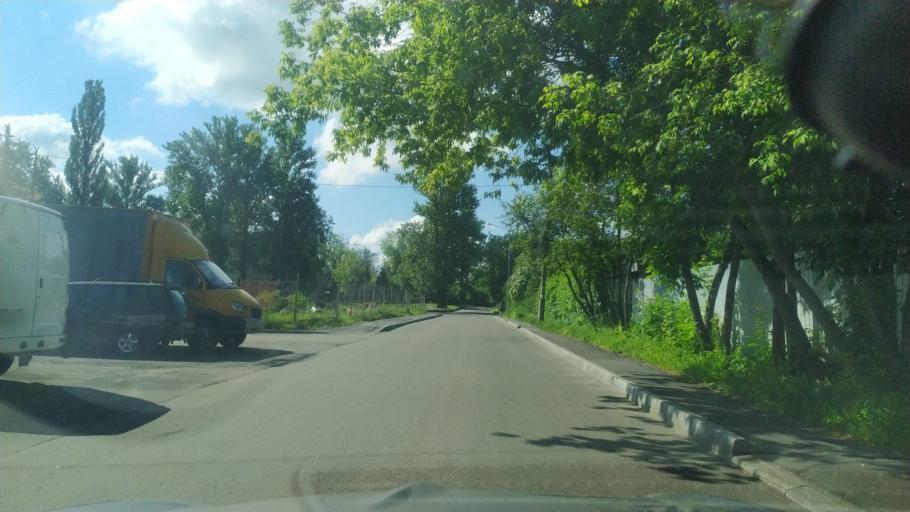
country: RU
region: Moscow
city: Vostochnyy
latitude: 55.8160
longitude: 37.8653
